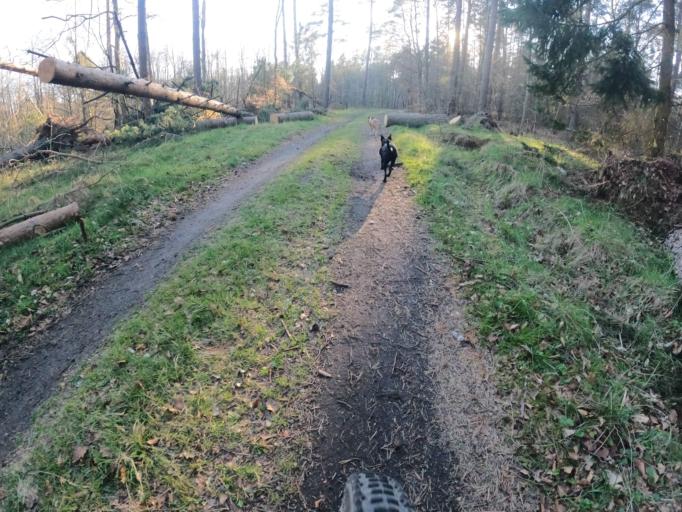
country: PL
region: West Pomeranian Voivodeship
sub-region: Powiat gryficki
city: Brojce
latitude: 53.9570
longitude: 15.4001
